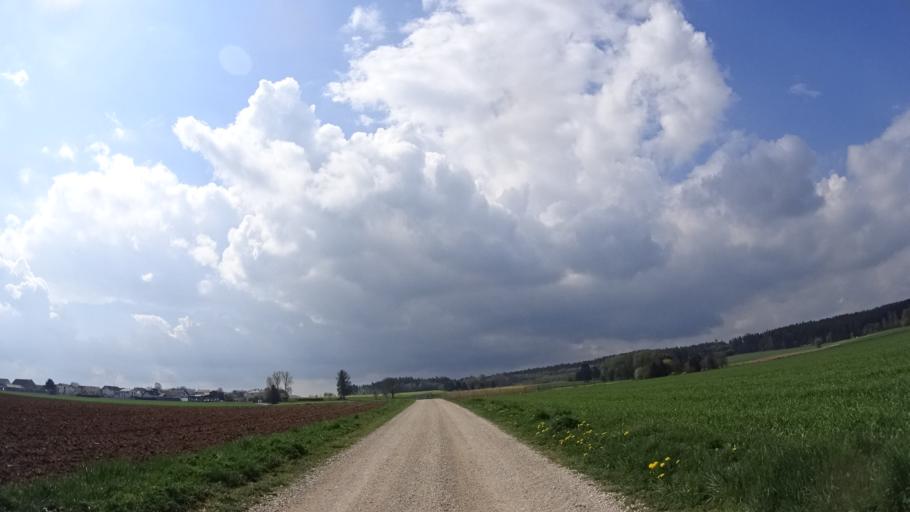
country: DE
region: Bavaria
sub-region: Upper Bavaria
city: Hitzhofen
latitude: 48.8577
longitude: 11.3081
